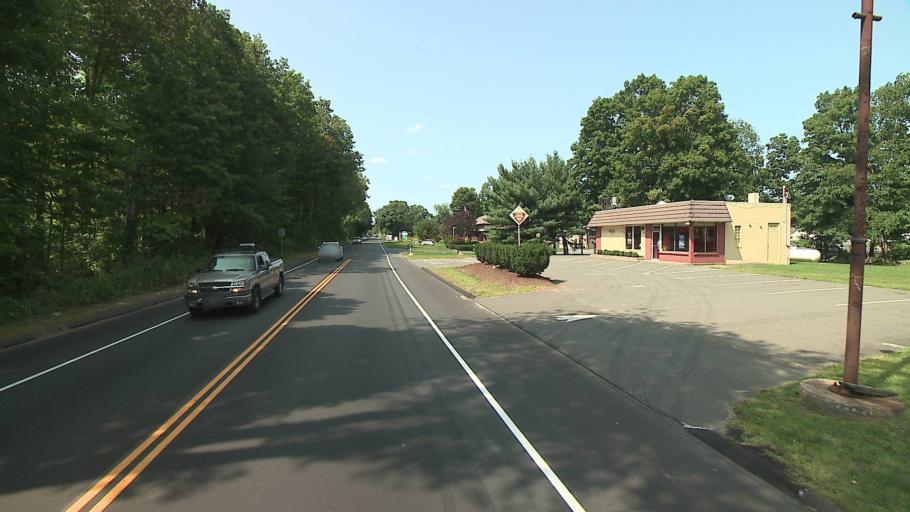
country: US
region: Connecticut
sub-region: Fairfield County
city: Trumbull
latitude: 41.2945
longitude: -73.2450
